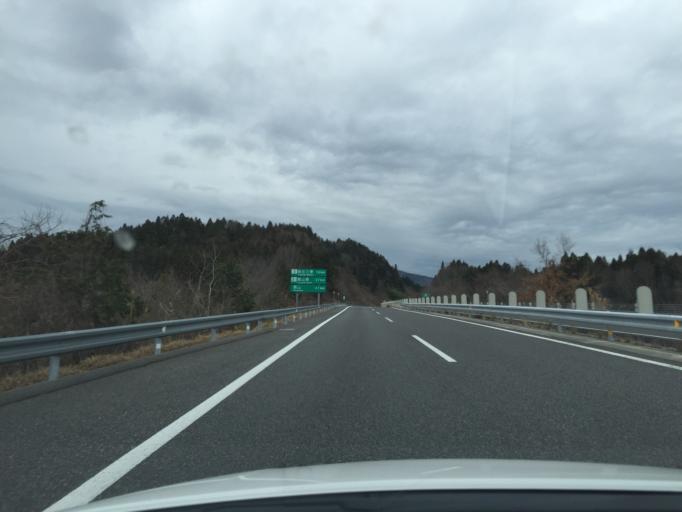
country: JP
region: Fukushima
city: Funehikimachi-funehiki
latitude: 37.3054
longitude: 140.6124
